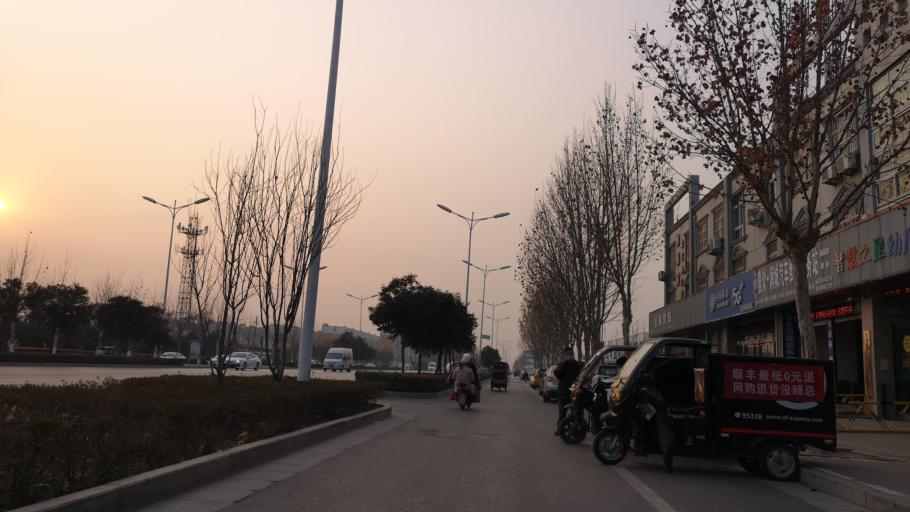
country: CN
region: Henan Sheng
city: Zhongyuanlu
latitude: 35.7890
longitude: 115.0927
